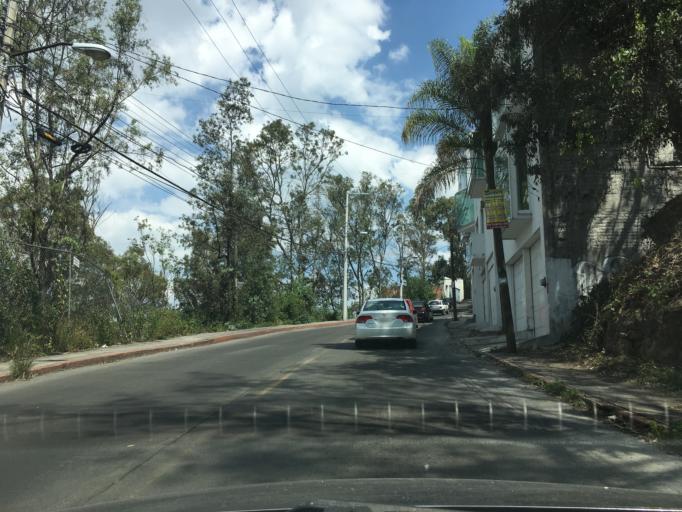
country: MX
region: Michoacan
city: Morelia
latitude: 19.6786
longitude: -101.1874
